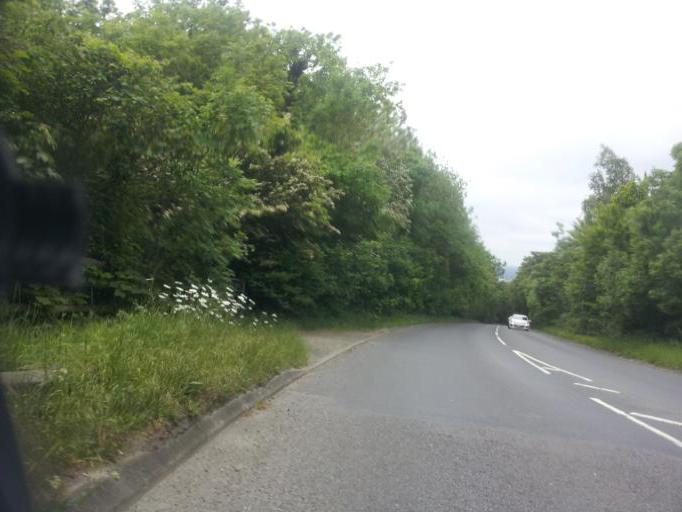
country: GB
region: England
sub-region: Kent
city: Aylesford
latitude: 51.3178
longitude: 0.5069
